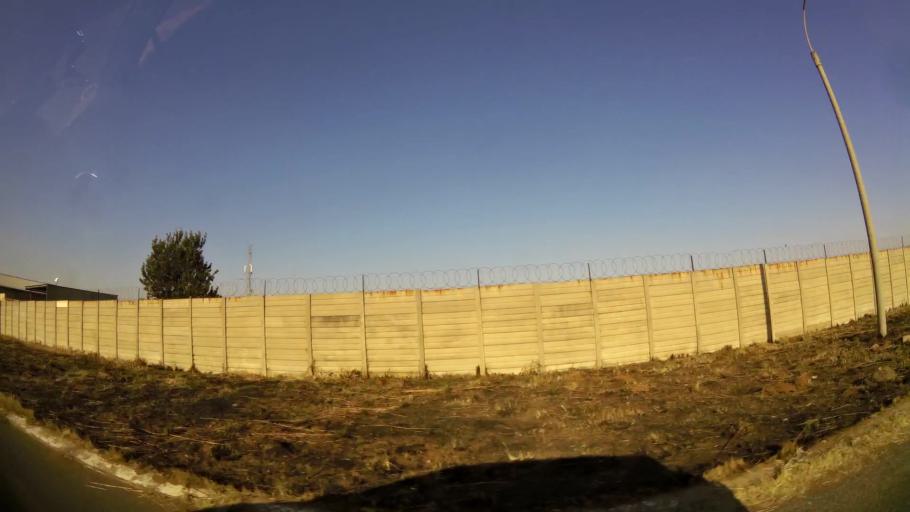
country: ZA
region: Gauteng
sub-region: West Rand District Municipality
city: Randfontein
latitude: -26.1987
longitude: 27.6898
